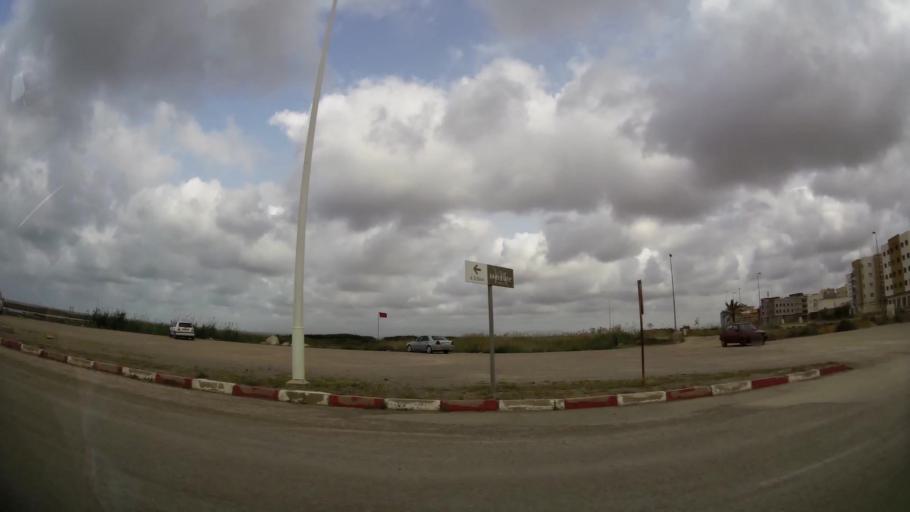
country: MA
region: Oriental
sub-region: Nador
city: Nador
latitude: 35.1537
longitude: -2.9071
